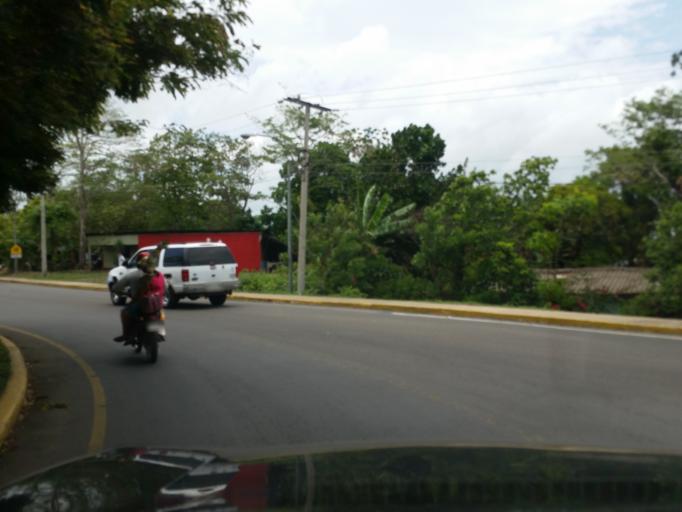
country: NI
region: Masaya
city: Catarina
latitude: 11.9105
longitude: -86.0785
